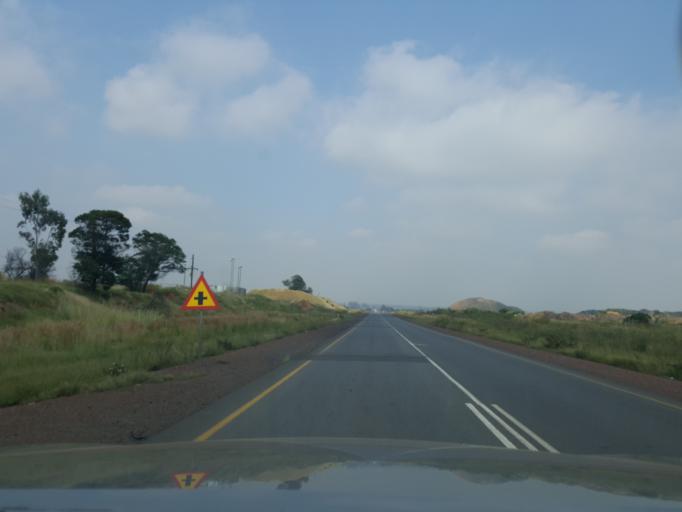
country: ZA
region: Mpumalanga
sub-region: Nkangala District Municipality
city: Witbank
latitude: -26.0146
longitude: 29.3918
